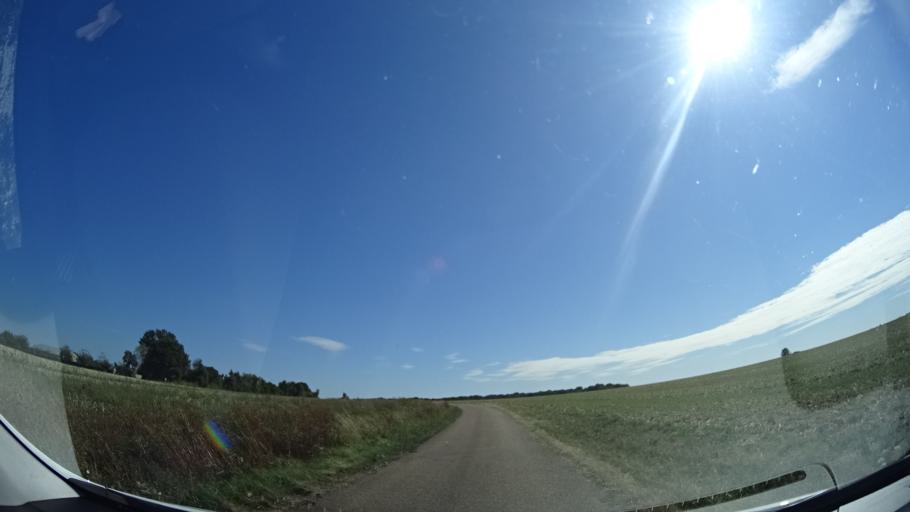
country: FR
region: Centre
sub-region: Departement du Loiret
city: Trigueres
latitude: 47.9571
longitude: 2.9677
